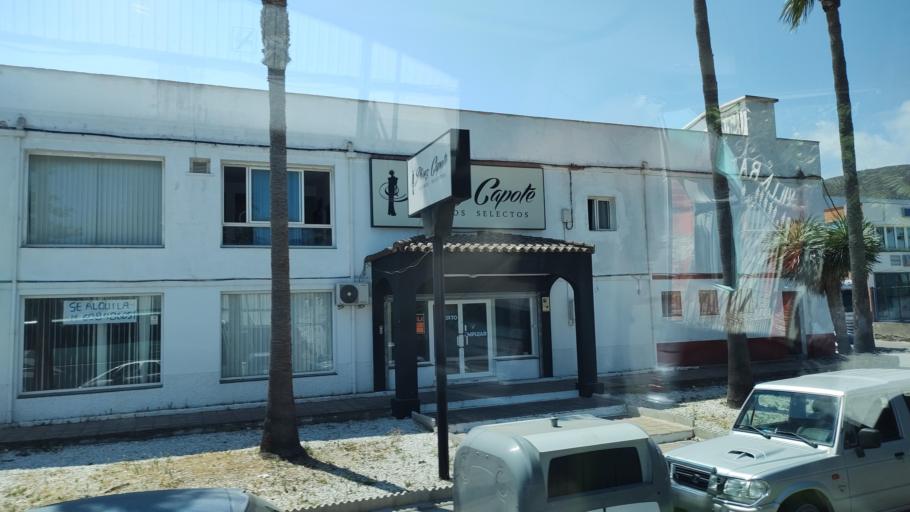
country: ES
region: Andalusia
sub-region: Provincia de Cadiz
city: La Linea de la Concepcion
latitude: 36.1852
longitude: -5.3497
